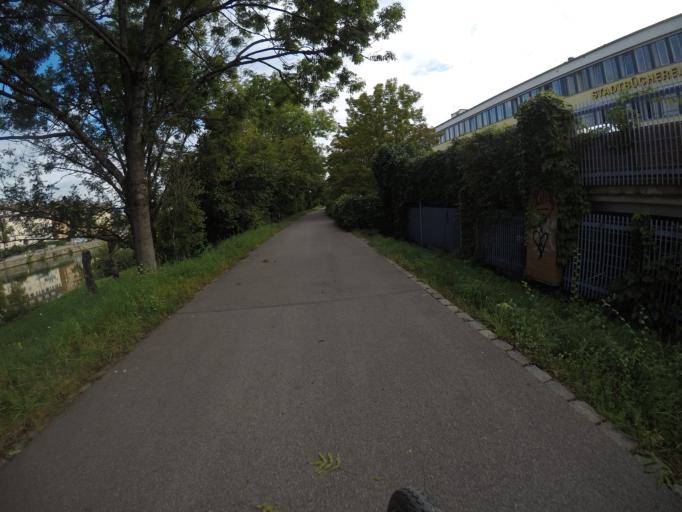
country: DE
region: Baden-Wuerttemberg
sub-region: Regierungsbezirk Stuttgart
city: Stuttgart-Ost
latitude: 48.8074
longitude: 9.2146
